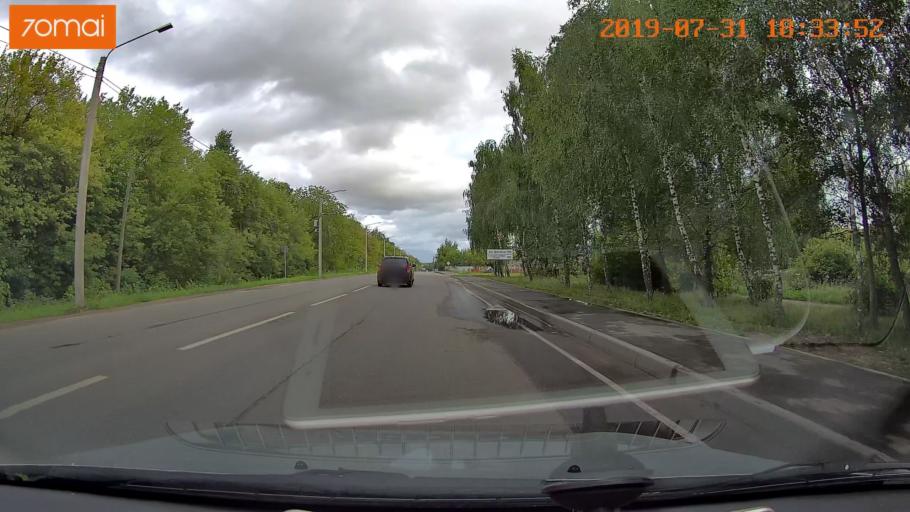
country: RU
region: Moskovskaya
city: Voskresensk
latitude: 55.3085
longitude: 38.6570
